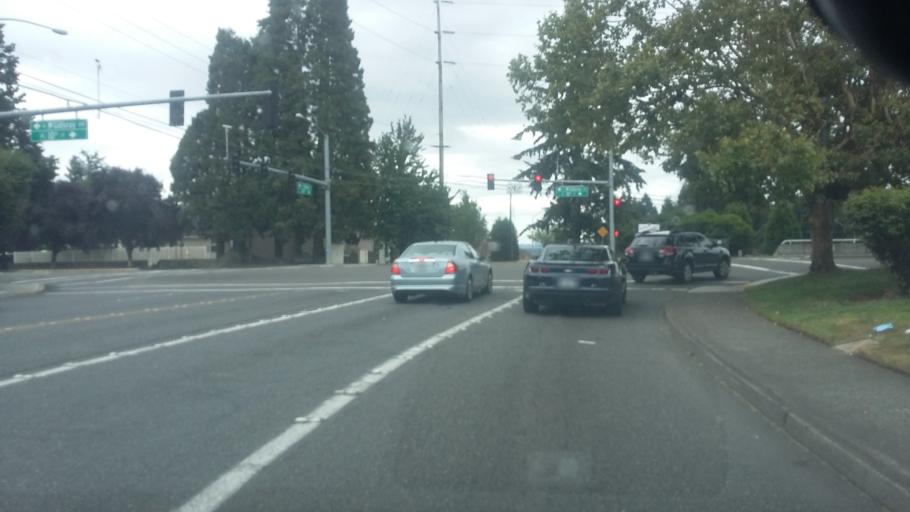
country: US
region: Washington
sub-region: Clark County
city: Orchards
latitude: 45.6151
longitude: -122.5537
